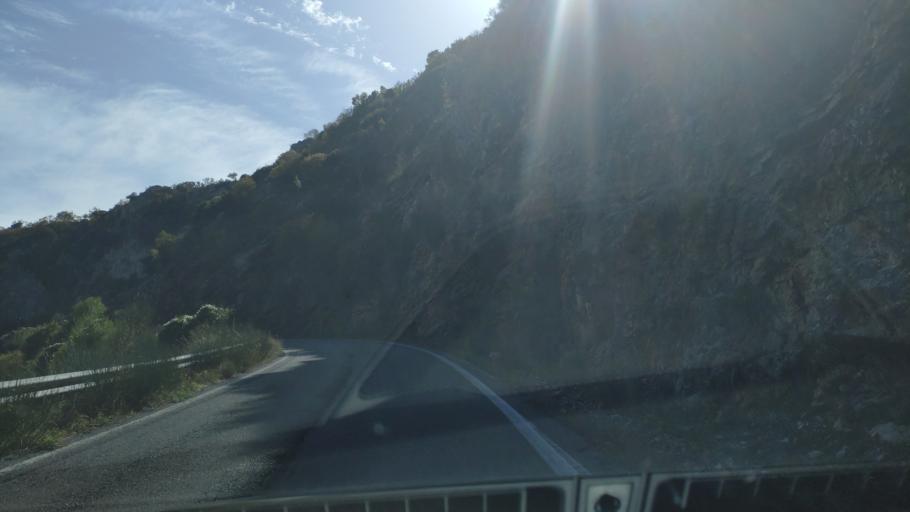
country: GR
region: Peloponnese
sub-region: Nomos Arkadias
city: Dimitsana
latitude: 37.5960
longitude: 22.0306
